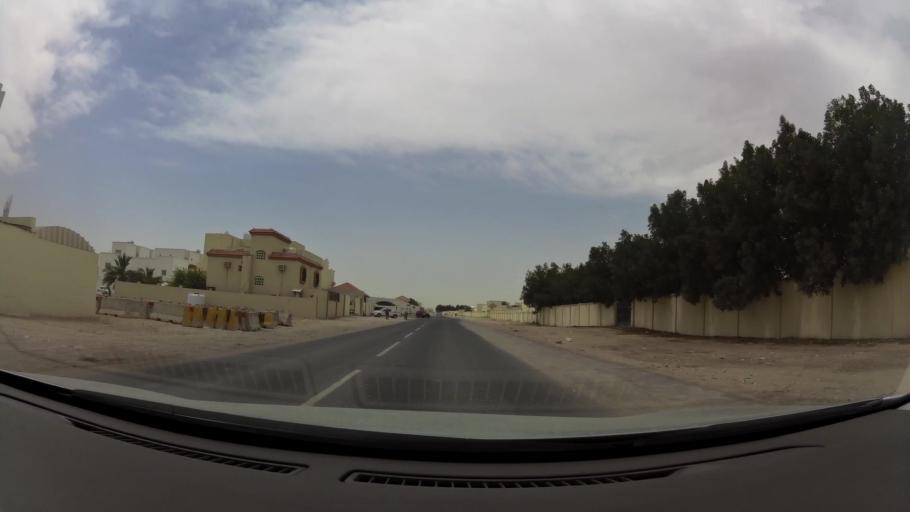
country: QA
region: Baladiyat ar Rayyan
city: Ar Rayyan
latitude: 25.2807
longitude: 51.4481
